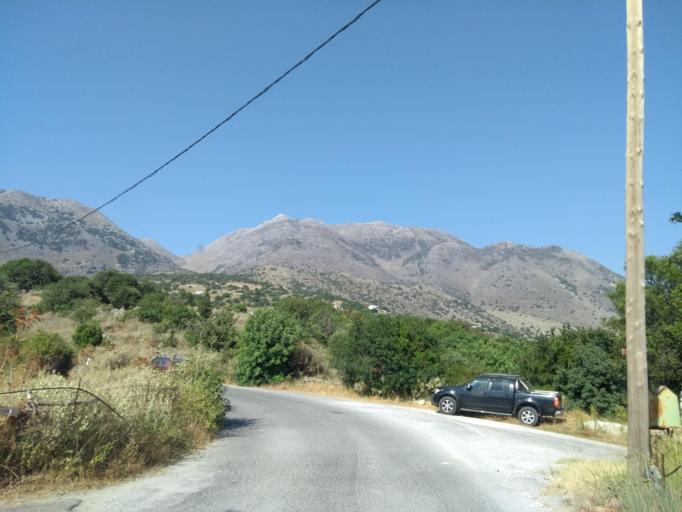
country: GR
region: Crete
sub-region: Nomos Chanias
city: Georgioupolis
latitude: 35.3188
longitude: 24.2967
